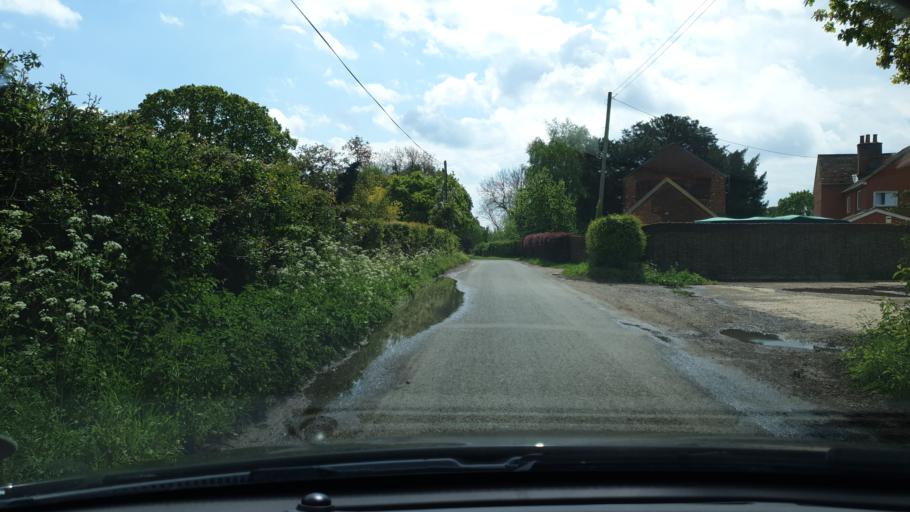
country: GB
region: England
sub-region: Essex
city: Great Bentley
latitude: 51.8730
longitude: 1.0616
